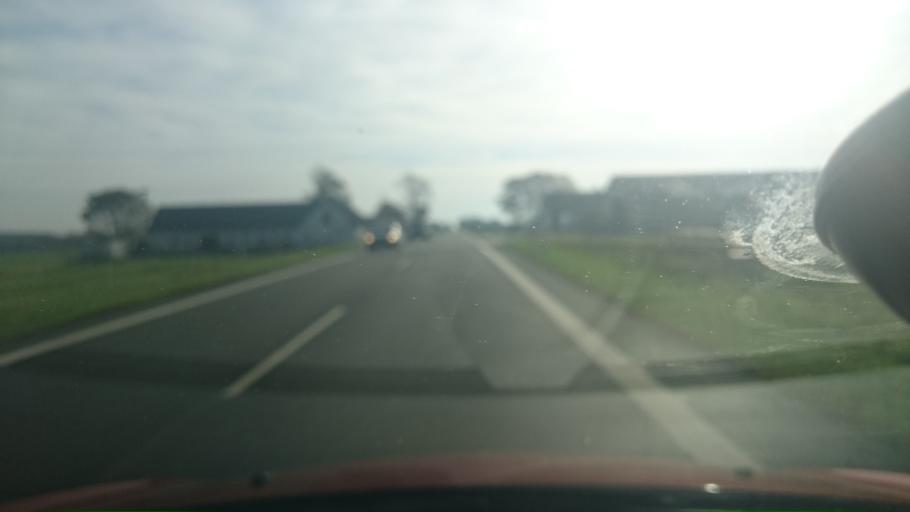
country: DK
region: Central Jutland
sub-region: Syddjurs Kommune
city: Hornslet
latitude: 56.3924
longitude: 10.2694
